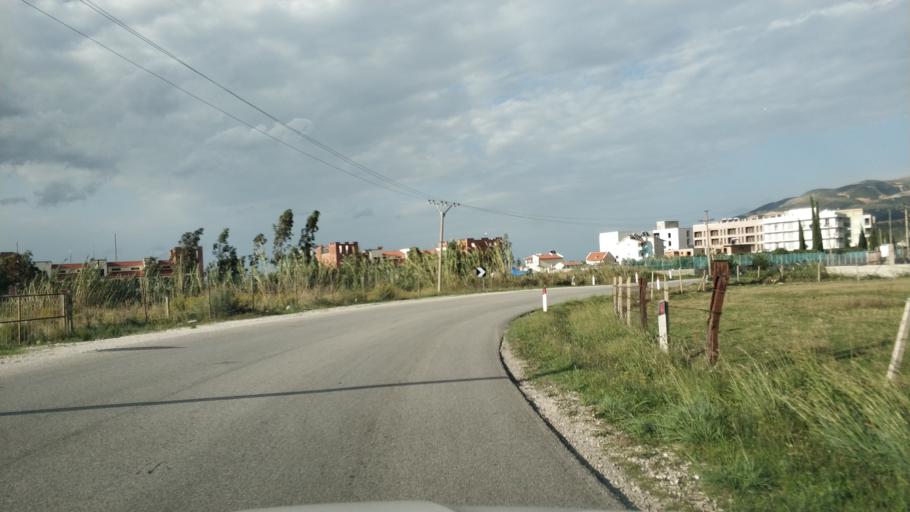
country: AL
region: Vlore
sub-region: Rrethi i Vlores
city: Orikum
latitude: 40.3372
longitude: 19.4753
